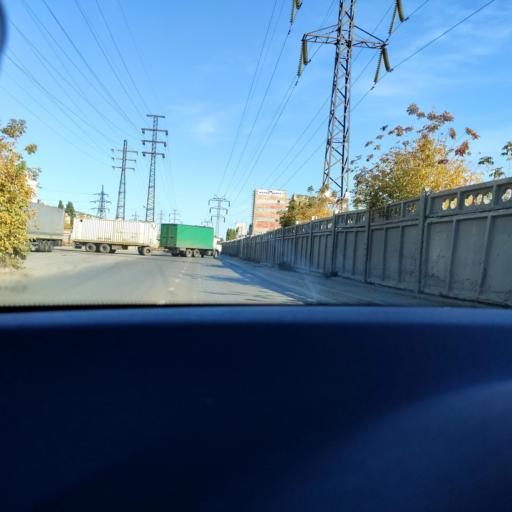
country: RU
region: Samara
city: Petra-Dubrava
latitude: 53.2456
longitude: 50.2922
